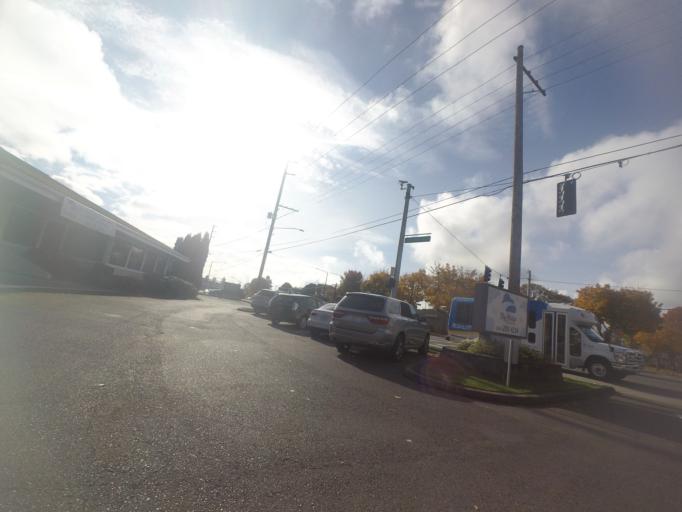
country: US
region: Washington
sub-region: Pierce County
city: Lakewood
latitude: 47.1734
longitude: -122.5181
